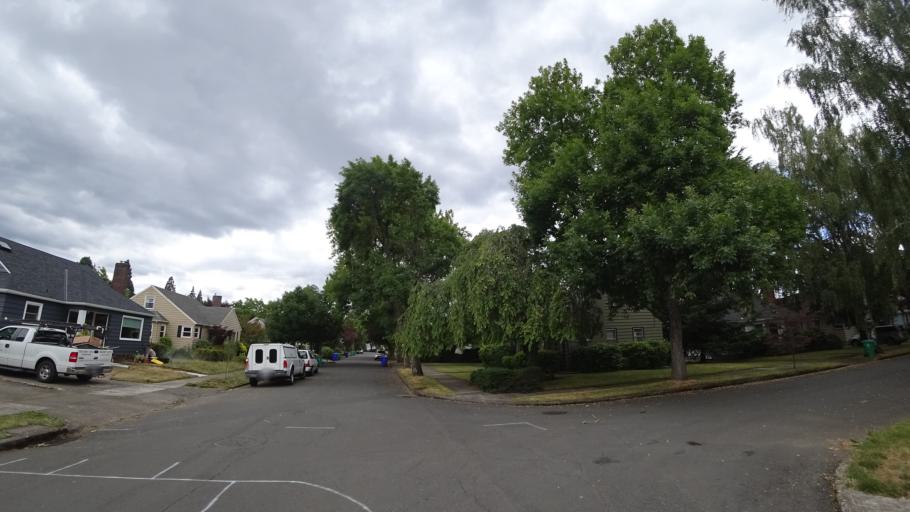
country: US
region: Oregon
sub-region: Multnomah County
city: Portland
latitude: 45.5757
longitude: -122.7169
